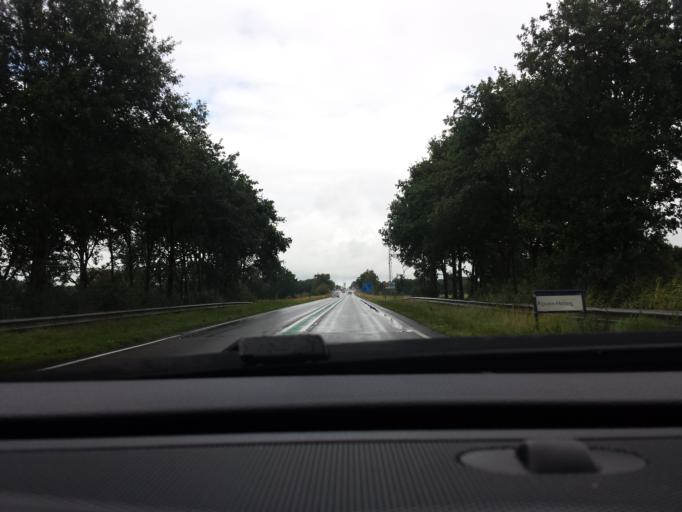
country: NL
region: Gelderland
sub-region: Gemeente Lochem
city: Laren
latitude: 52.2432
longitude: 6.3988
